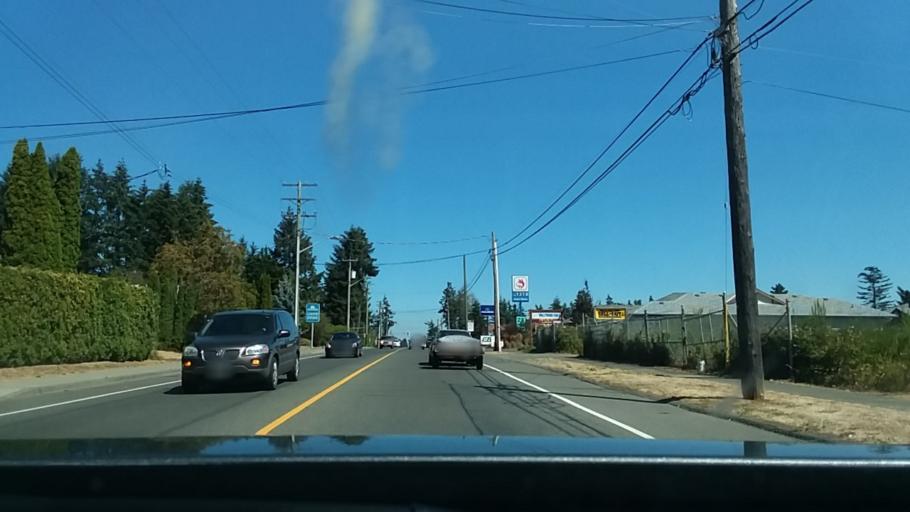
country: CA
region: British Columbia
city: Courtenay
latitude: 49.6858
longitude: -124.9350
